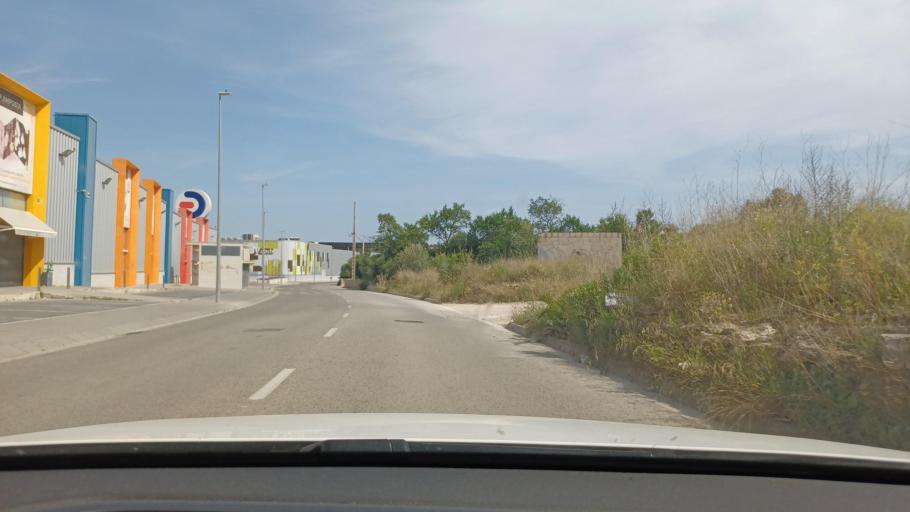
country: ES
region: Catalonia
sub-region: Provincia de Tarragona
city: Amposta
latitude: 40.7088
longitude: 0.5687
